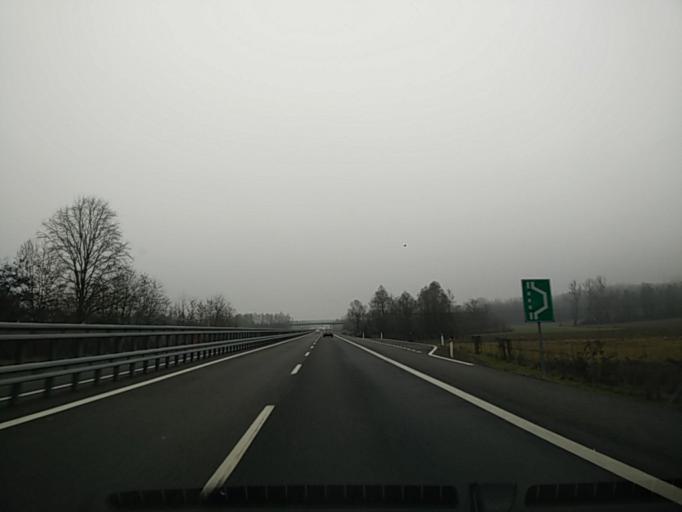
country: IT
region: Piedmont
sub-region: Provincia di Asti
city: Dusino
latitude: 44.9325
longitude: 7.9996
